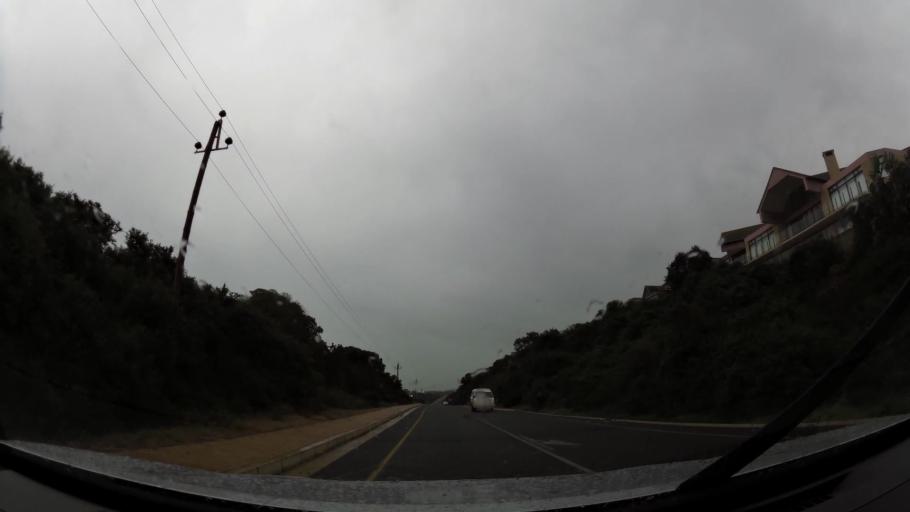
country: ZA
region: Western Cape
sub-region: Eden District Municipality
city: George
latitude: -34.0491
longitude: 22.2884
